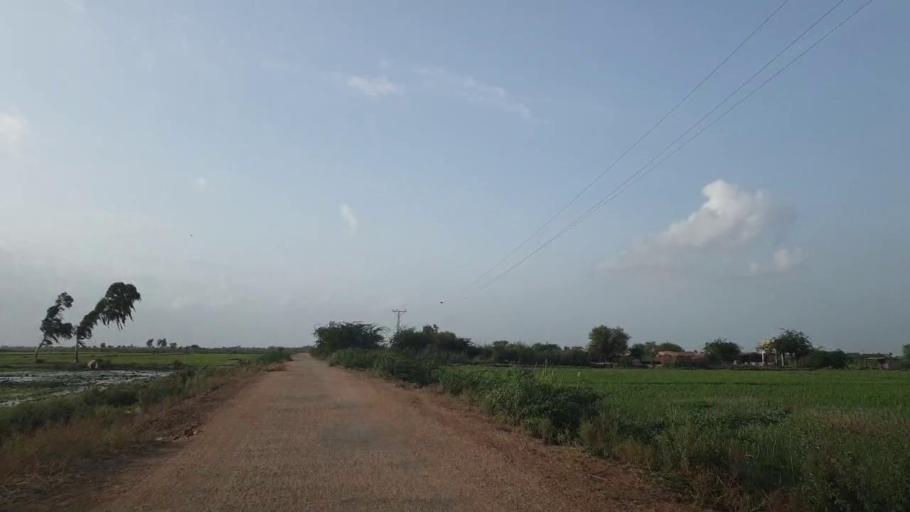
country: PK
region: Sindh
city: Tando Bago
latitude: 24.6588
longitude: 69.1119
